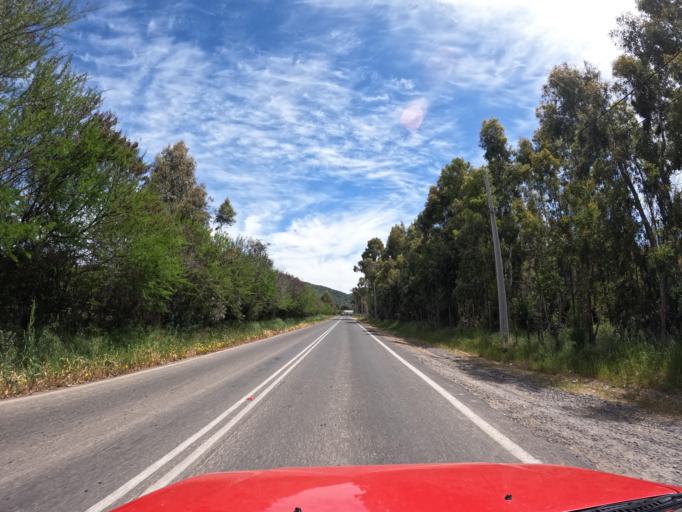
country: CL
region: Maule
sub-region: Provincia de Talca
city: Talca
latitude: -35.1166
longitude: -71.6421
